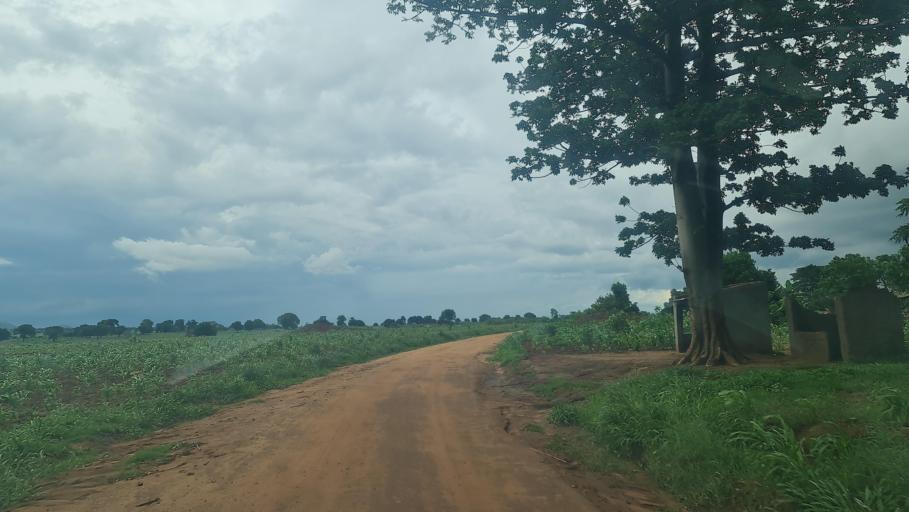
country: MW
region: Southern Region
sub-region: Nsanje District
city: Nsanje
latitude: -17.3940
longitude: 35.5721
